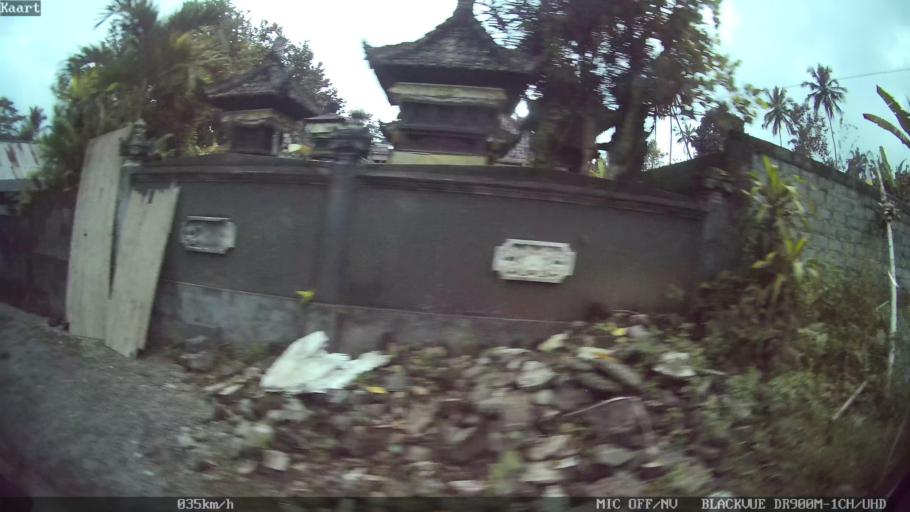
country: ID
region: Bali
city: Banjar Geriana Kangin
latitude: -8.4001
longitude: 115.4402
